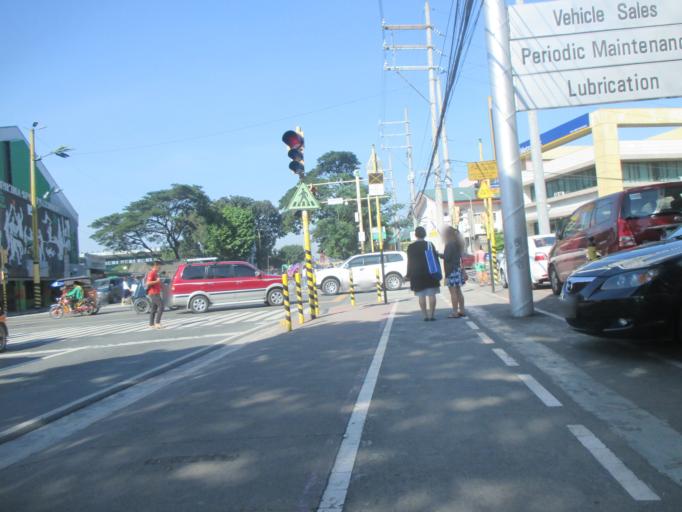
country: PH
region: Metro Manila
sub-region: Marikina
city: Calumpang
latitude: 14.6355
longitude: 121.0996
